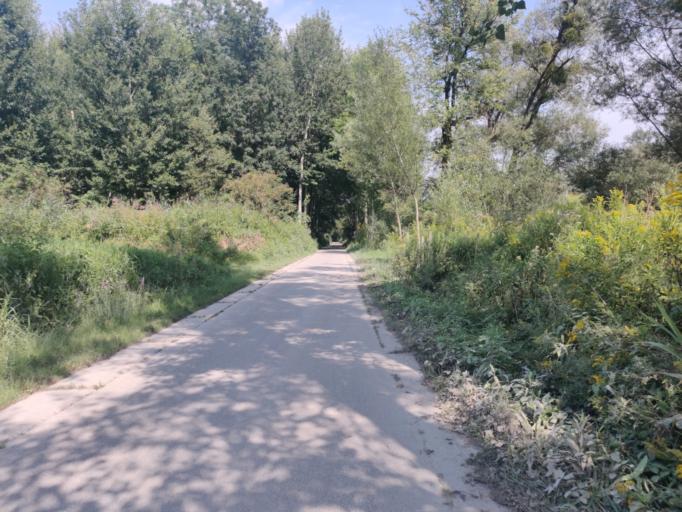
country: AT
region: Lower Austria
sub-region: Politischer Bezirk Amstetten
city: Zeillern
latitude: 48.1860
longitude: 14.7934
